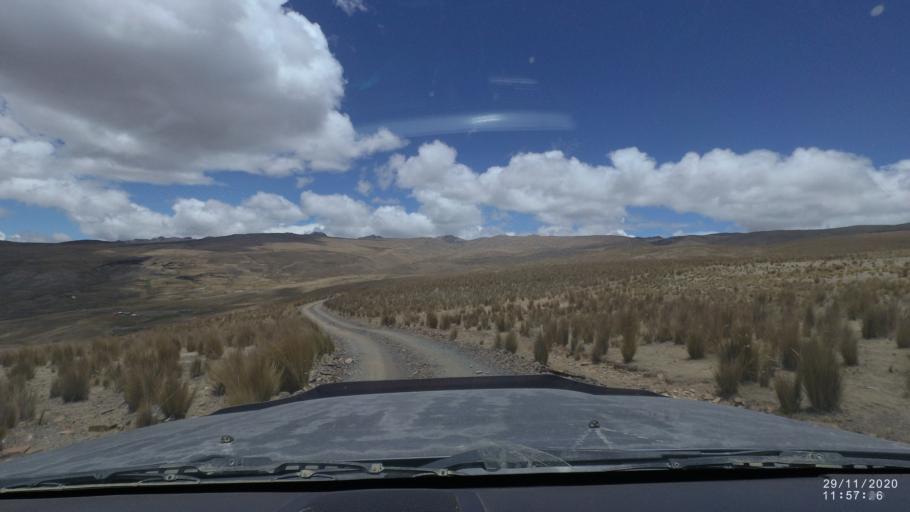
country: BO
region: Cochabamba
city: Cochabamba
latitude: -17.1586
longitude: -66.2738
